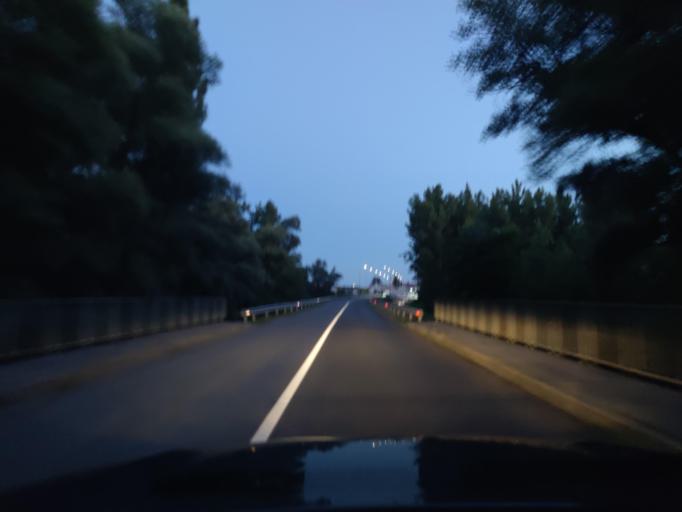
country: HR
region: Medimurska
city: Peklenica
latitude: 46.5171
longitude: 16.4410
